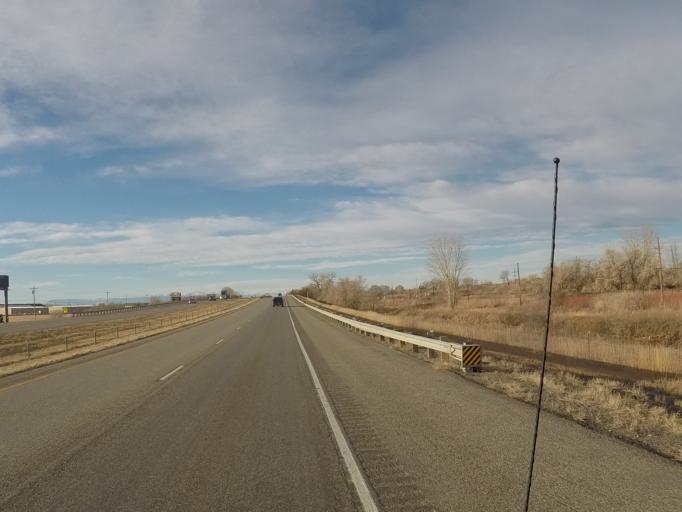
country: US
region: Montana
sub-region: Yellowstone County
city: Laurel
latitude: 45.7076
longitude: -108.6544
